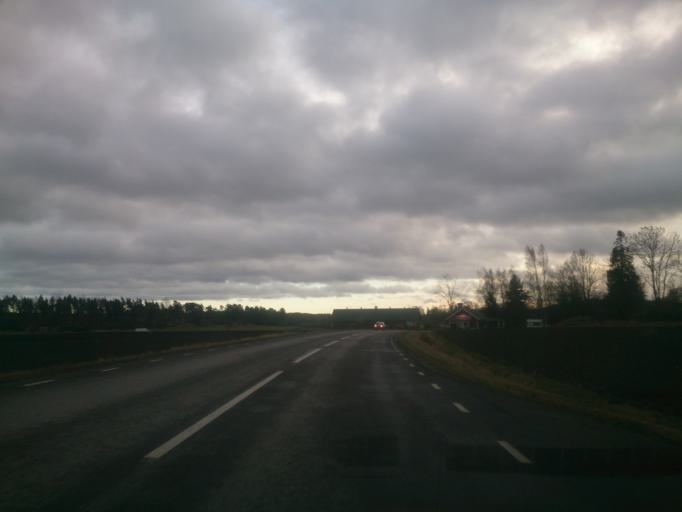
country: SE
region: OEstergoetland
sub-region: Norrkopings Kommun
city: Krokek
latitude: 58.5806
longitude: 16.5666
